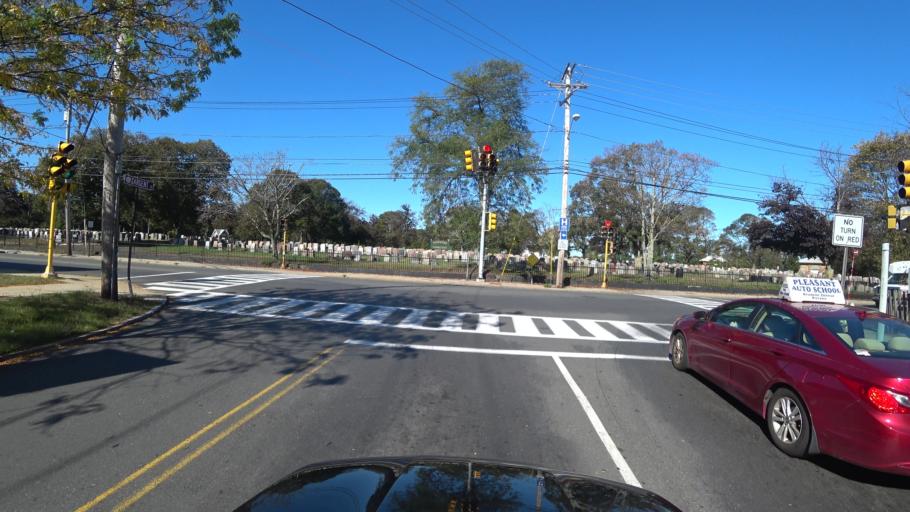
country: US
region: Massachusetts
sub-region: Suffolk County
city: Revere
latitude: 42.4218
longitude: -71.0292
